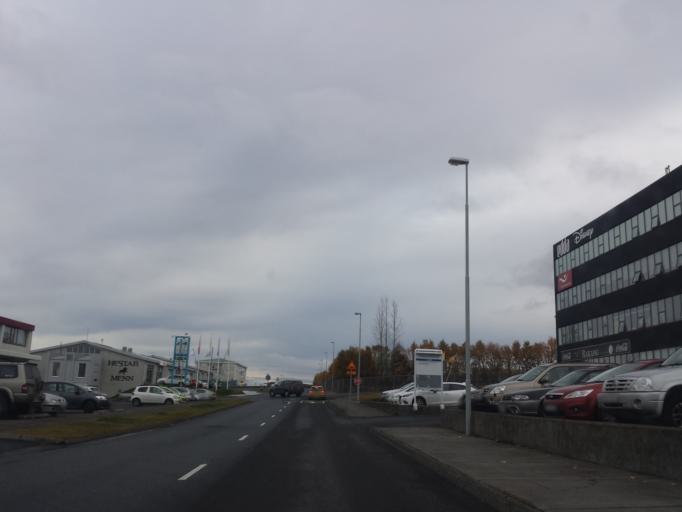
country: IS
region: Capital Region
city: Reykjavik
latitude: 64.1206
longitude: -21.7944
